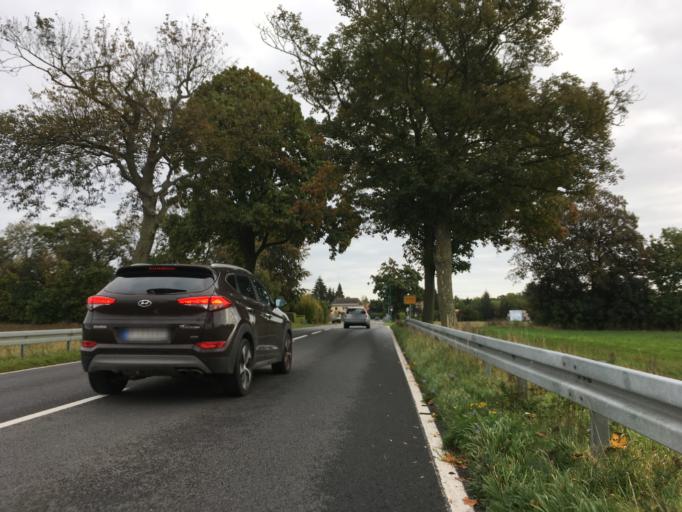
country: DE
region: Brandenburg
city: Protzel
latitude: 52.7058
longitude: 13.9112
